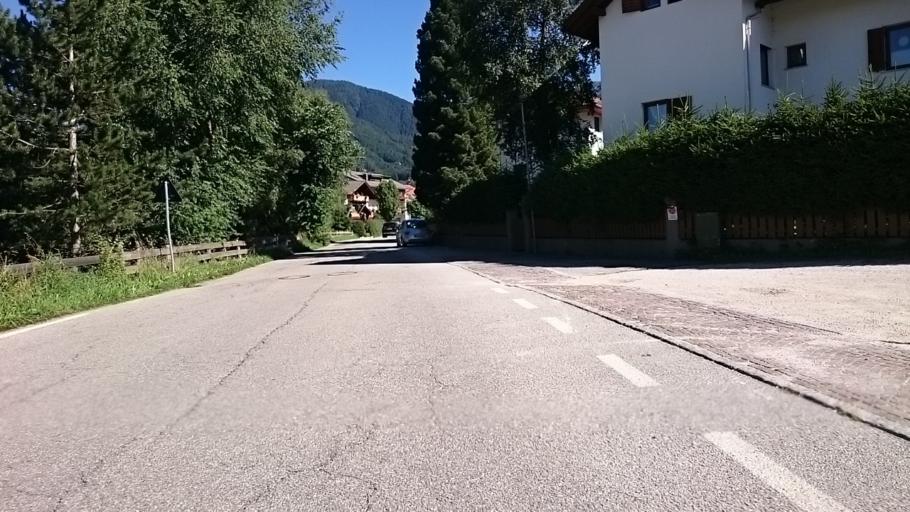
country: IT
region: Trentino-Alto Adige
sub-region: Bolzano
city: Valdaora di Mezzo
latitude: 46.7627
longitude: 12.0282
